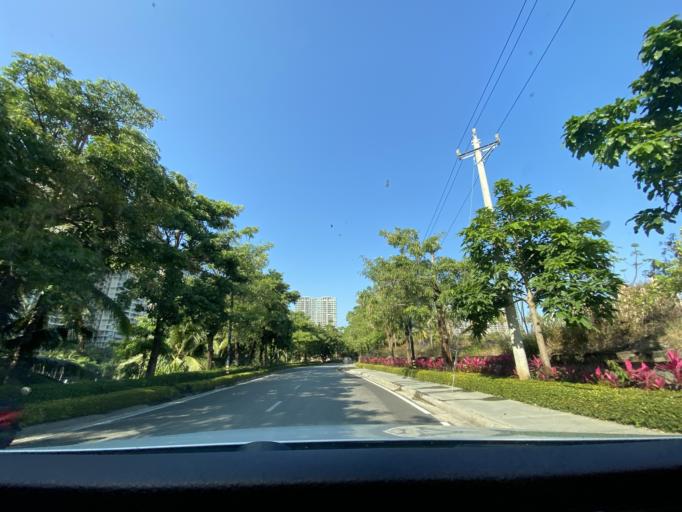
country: CN
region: Hainan
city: Yingzhou
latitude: 18.4104
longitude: 109.8815
